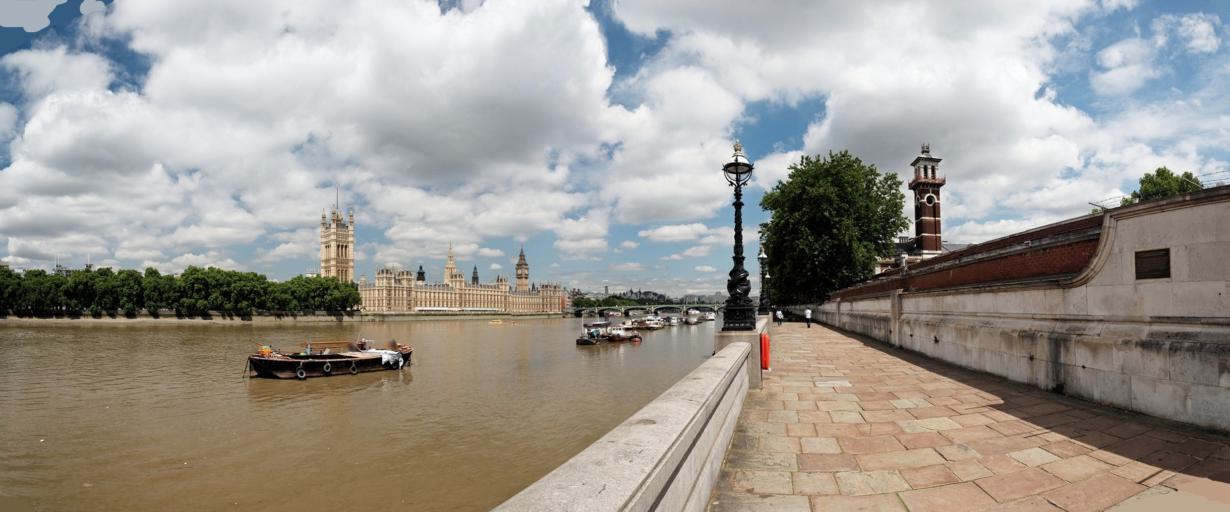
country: GB
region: England
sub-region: Greater London
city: City of Westminster
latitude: 51.4958
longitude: -0.1220
